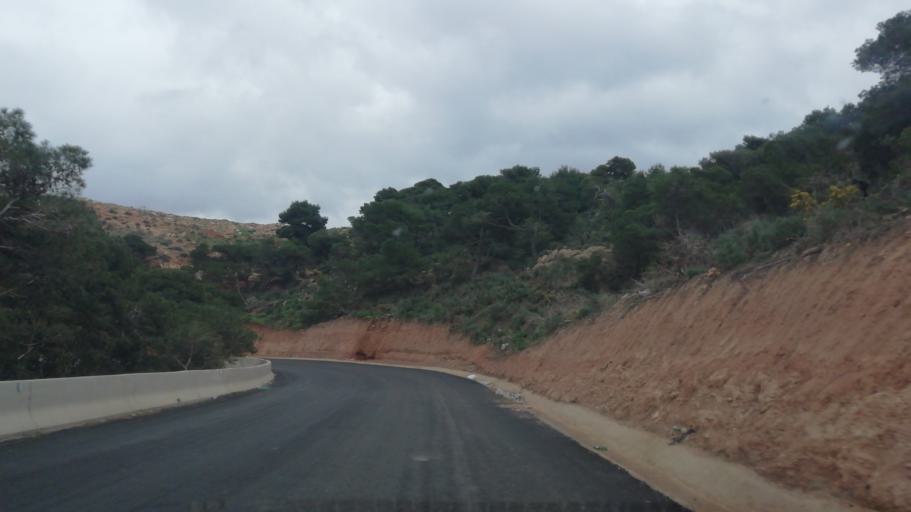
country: DZ
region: Oran
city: Bir el Djir
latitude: 35.7615
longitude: -0.5301
